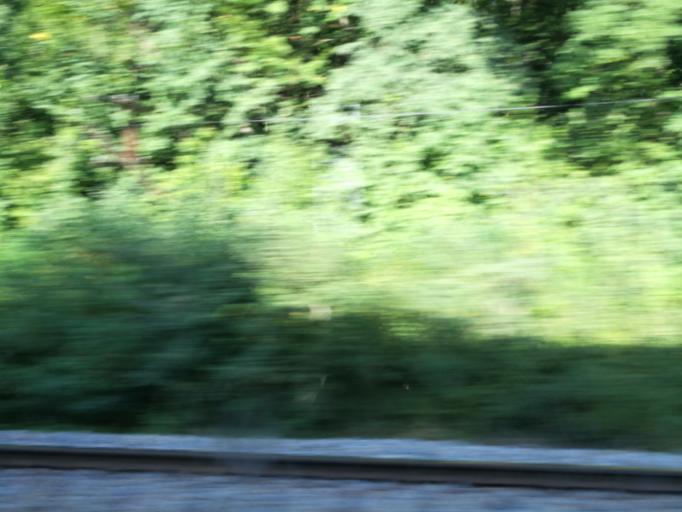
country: RO
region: Iasi
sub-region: Comuna Grajduri
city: Grajduri
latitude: 46.9949
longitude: 27.5448
